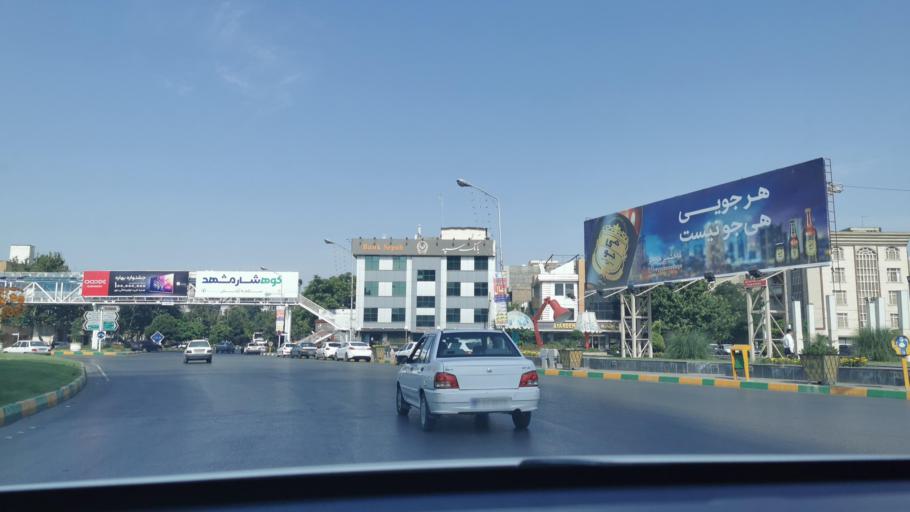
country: IR
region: Razavi Khorasan
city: Mashhad
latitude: 36.3249
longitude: 59.5634
